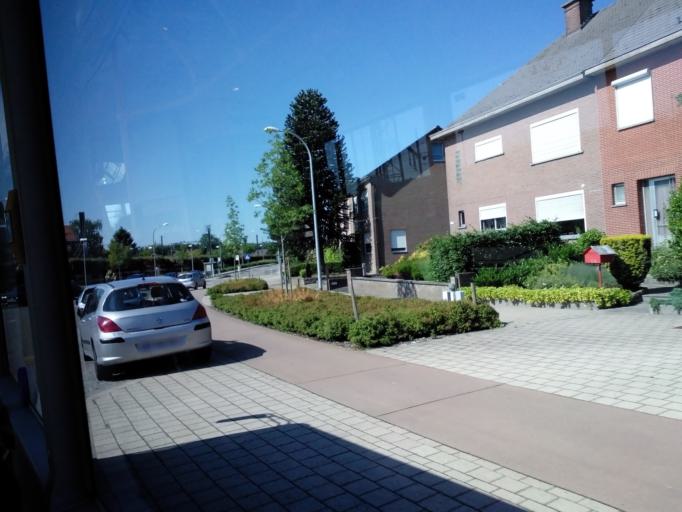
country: BE
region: Flanders
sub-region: Provincie Vlaams-Brabant
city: Leuven
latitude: 50.9064
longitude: 4.7195
